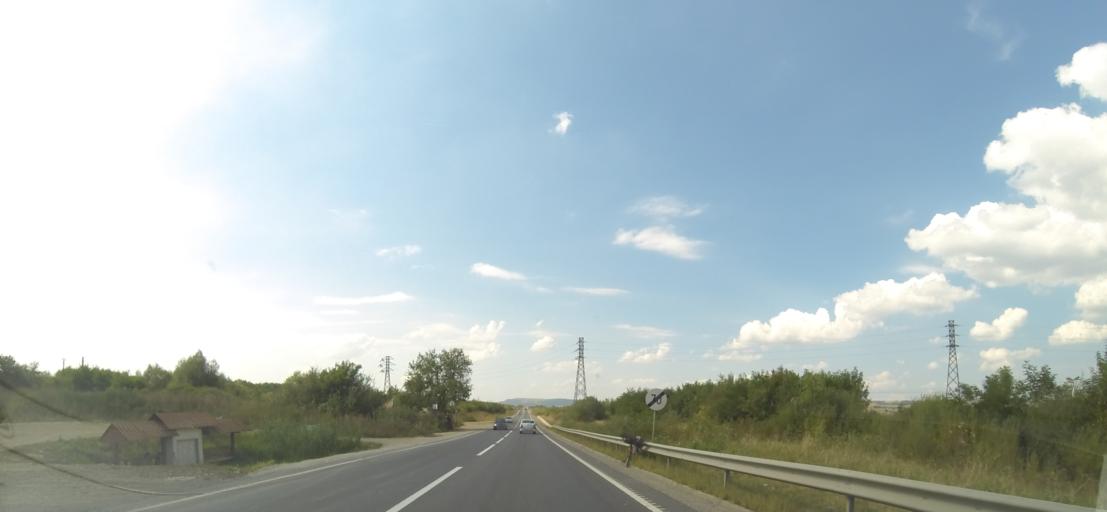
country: RO
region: Brasov
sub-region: Comuna Mandra
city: Mandra
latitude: 45.8261
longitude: 25.0350
